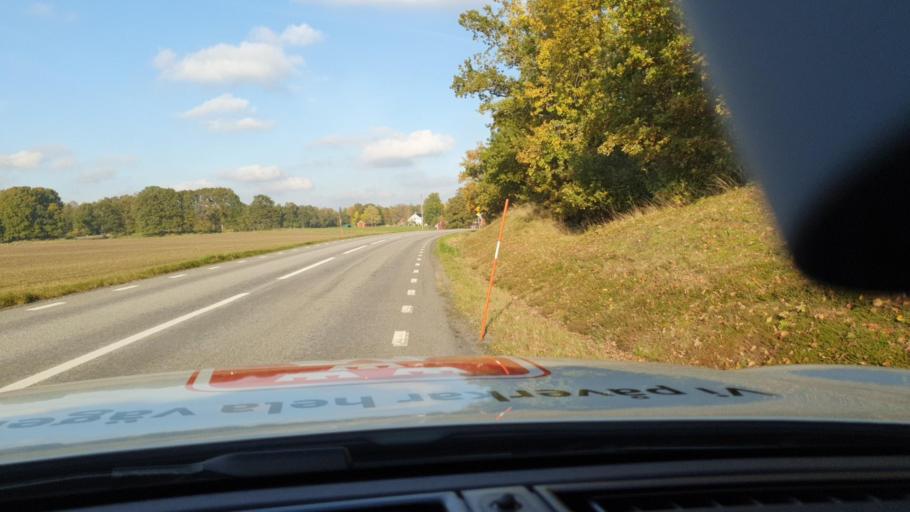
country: SE
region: Kronoberg
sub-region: Ljungby Kommun
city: Ljungby
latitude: 56.8209
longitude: 13.8022
